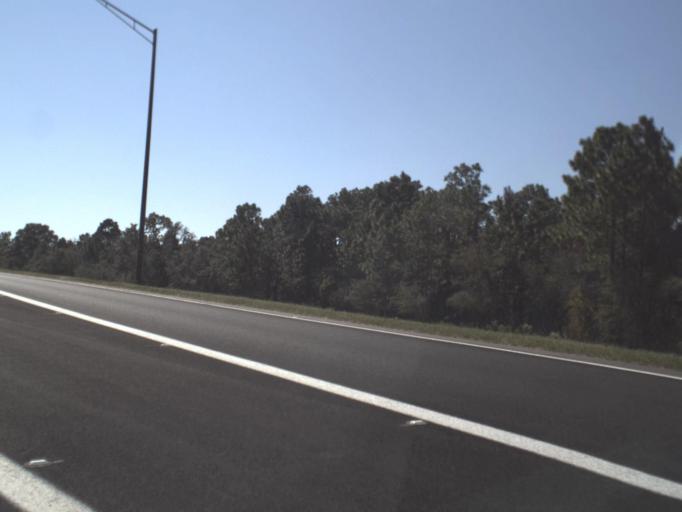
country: US
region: Florida
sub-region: Hernando County
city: Spring Hill
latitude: 28.4846
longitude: -82.4838
